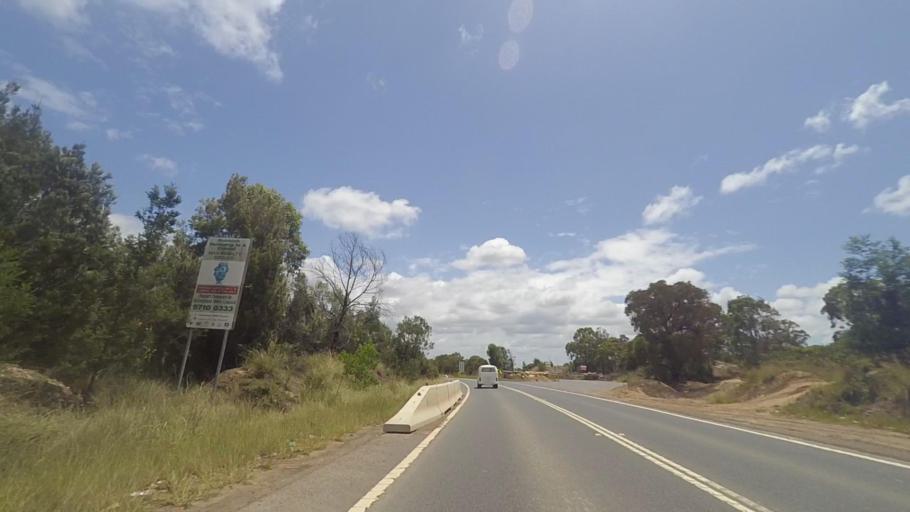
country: AU
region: New South Wales
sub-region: Liverpool
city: East Hills
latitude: -33.9938
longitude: 150.9968
